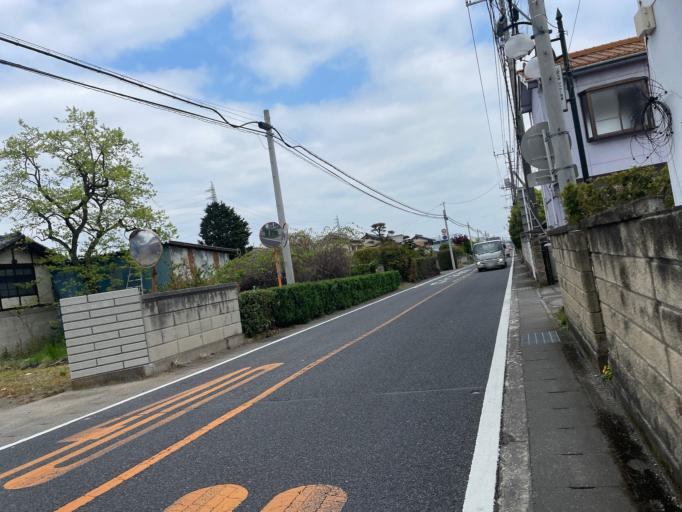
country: JP
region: Gunma
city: Isesaki
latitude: 36.2889
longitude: 139.1746
